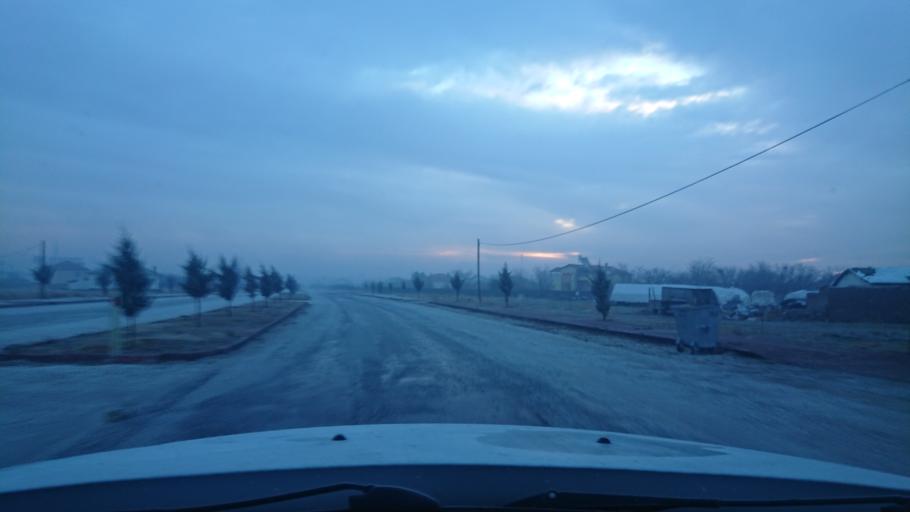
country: TR
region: Aksaray
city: Sultanhani
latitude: 38.2482
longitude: 33.5378
